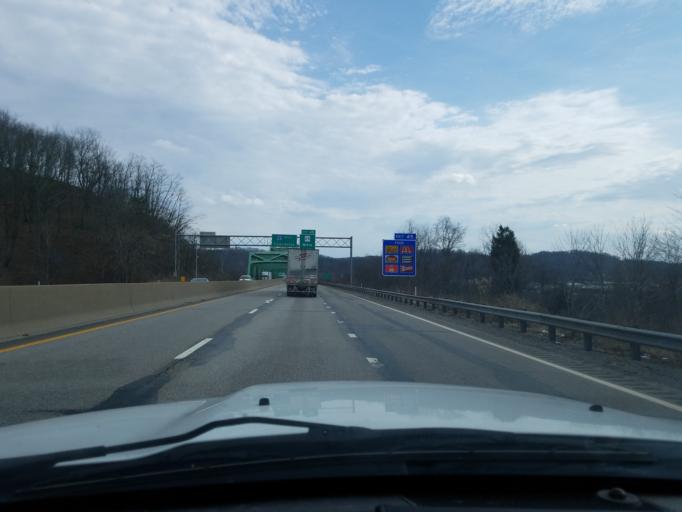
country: US
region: West Virginia
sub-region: Kanawha County
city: Nitro
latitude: 38.4467
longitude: -81.8463
